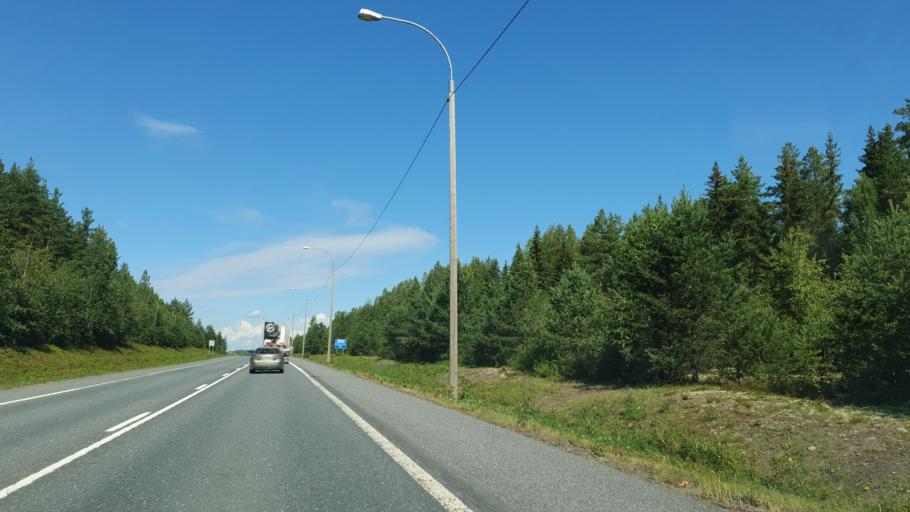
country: FI
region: Northern Savo
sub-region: Ylae-Savo
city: Iisalmi
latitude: 63.5806
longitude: 27.2344
